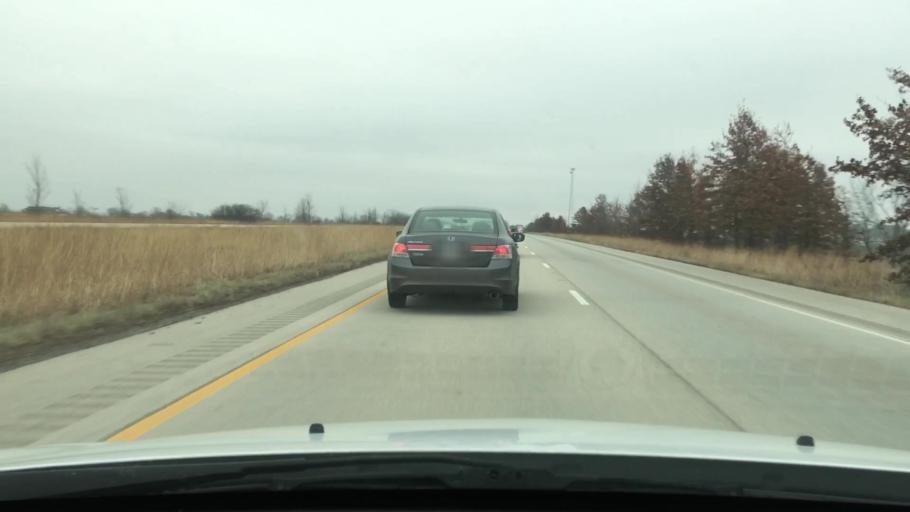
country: US
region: Illinois
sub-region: Sangamon County
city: New Berlin
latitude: 39.7405
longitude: -89.8812
